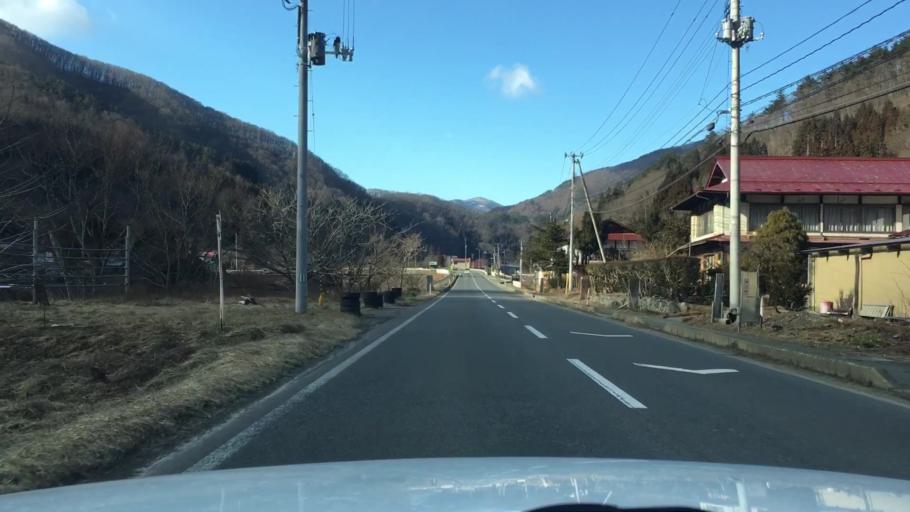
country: JP
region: Iwate
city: Tono
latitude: 39.6125
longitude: 141.6298
